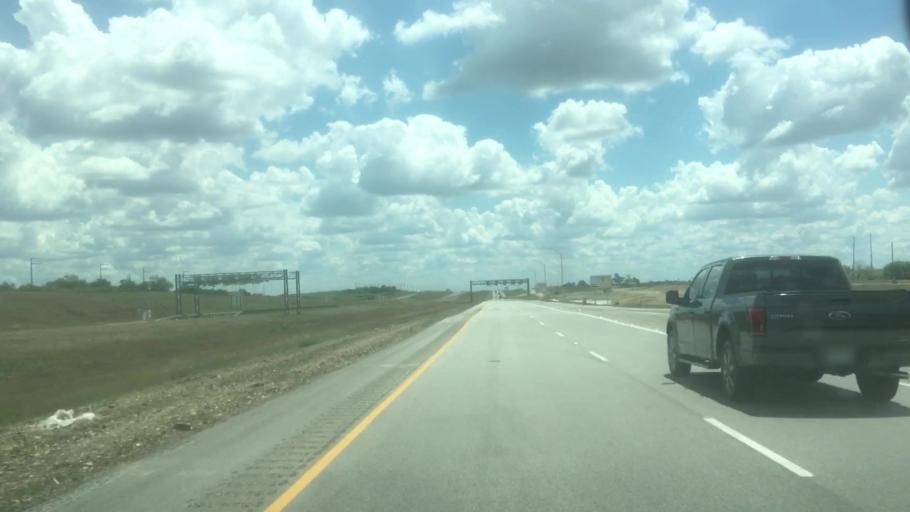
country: US
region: Texas
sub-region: Caldwell County
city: Uhland
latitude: 29.9928
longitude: -97.6850
